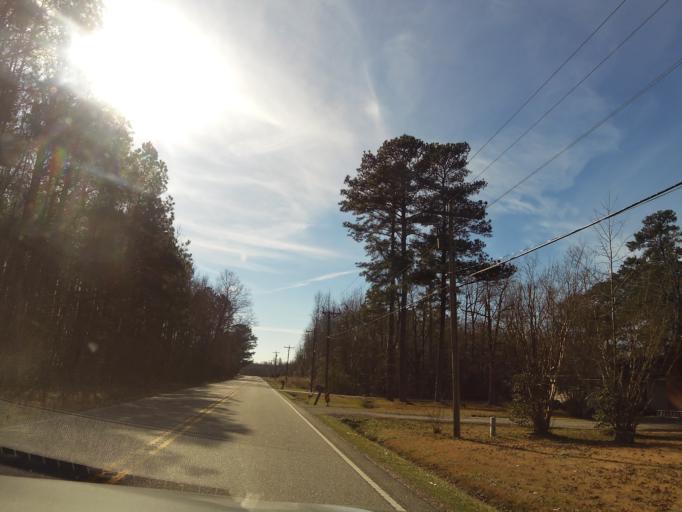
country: US
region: Virginia
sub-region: Isle of Wight County
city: Smithfield
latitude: 36.9572
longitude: -76.6704
